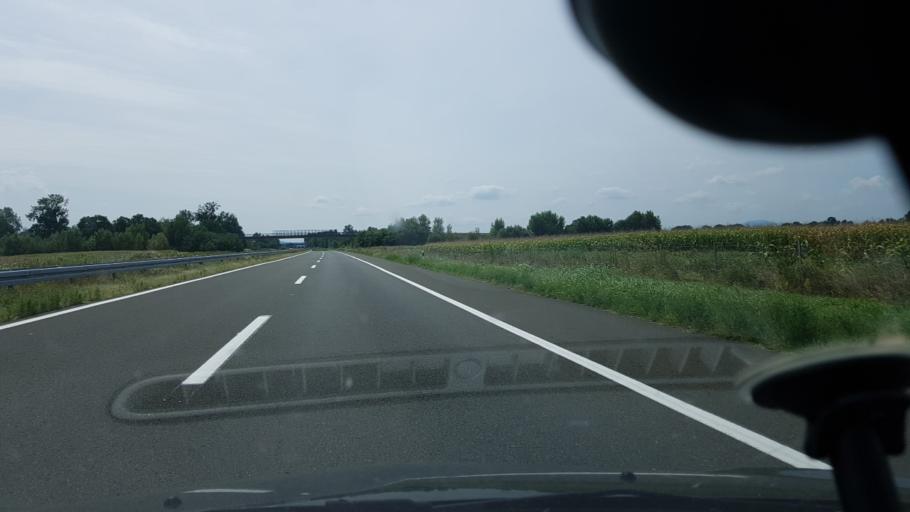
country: HR
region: Medimurska
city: Mala Subotica
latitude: 46.3647
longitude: 16.5417
